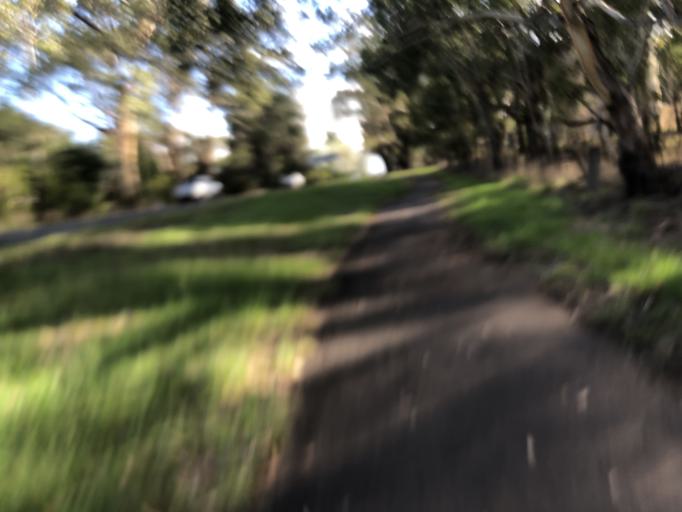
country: AU
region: New South Wales
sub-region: Orange Municipality
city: Orange
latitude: -33.3218
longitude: 149.0868
